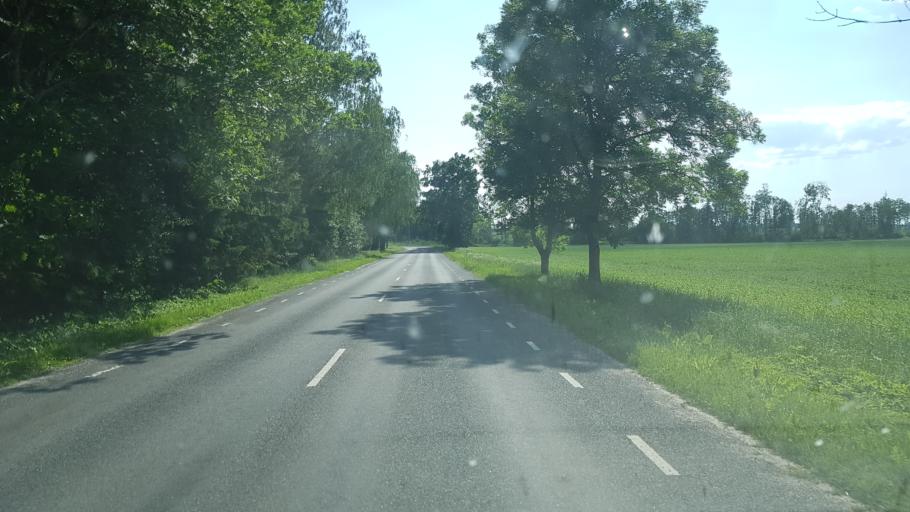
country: EE
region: Jaervamaa
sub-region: Koeru vald
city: Koeru
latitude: 58.9752
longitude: 26.0395
